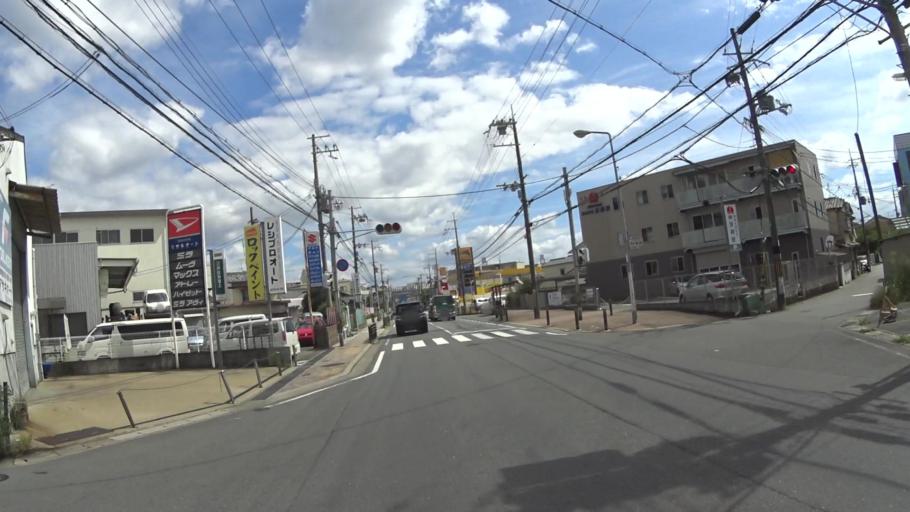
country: JP
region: Kyoto
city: Yawata
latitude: 34.8780
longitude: 135.7405
